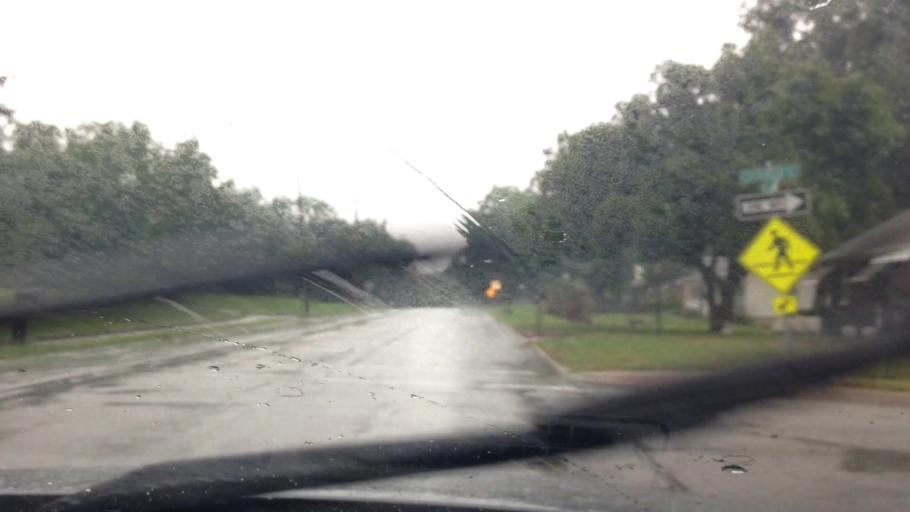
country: US
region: Kansas
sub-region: Leavenworth County
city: Leavenworth
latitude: 39.2940
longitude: -94.9183
